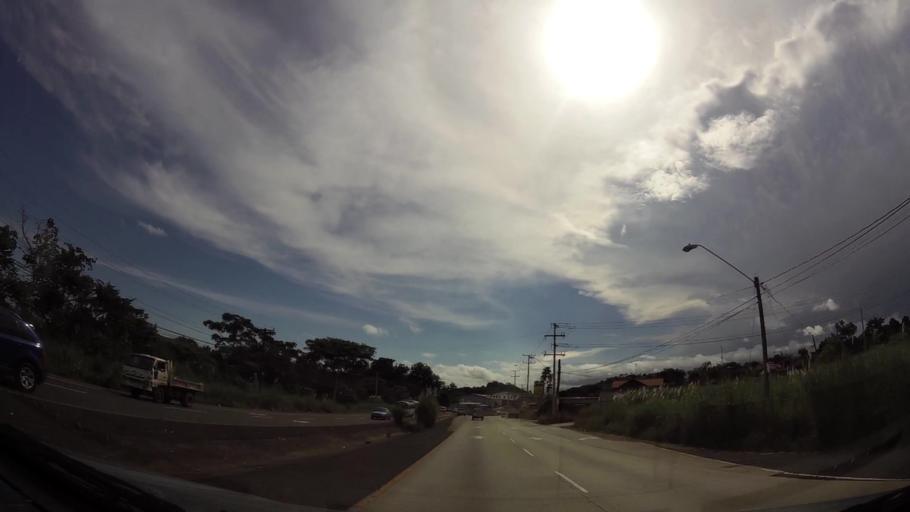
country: PA
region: Panama
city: La Chorrera
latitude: 8.8970
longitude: -79.7587
